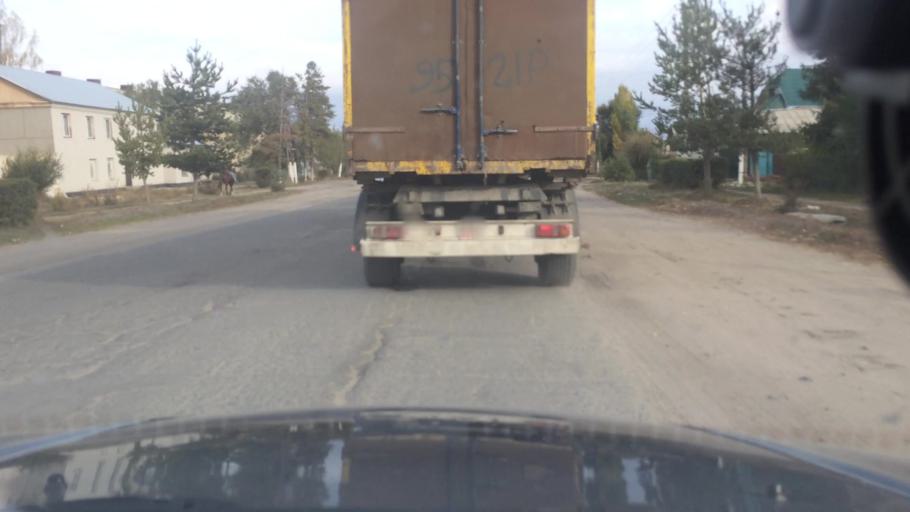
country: KG
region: Ysyk-Koel
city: Karakol
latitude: 42.5143
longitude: 78.3858
